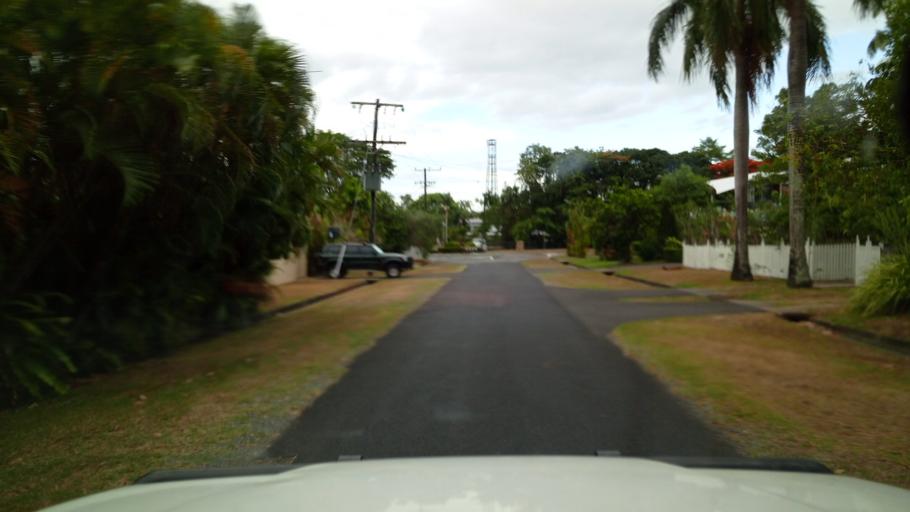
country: AU
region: Queensland
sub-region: Cairns
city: Redlynch
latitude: -16.8792
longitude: 145.7243
